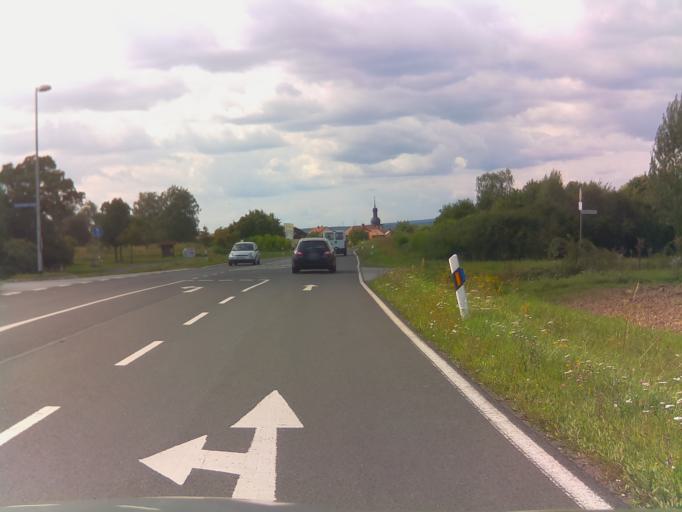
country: DE
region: Bavaria
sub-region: Regierungsbezirk Unterfranken
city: Sand
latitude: 49.9861
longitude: 10.5973
